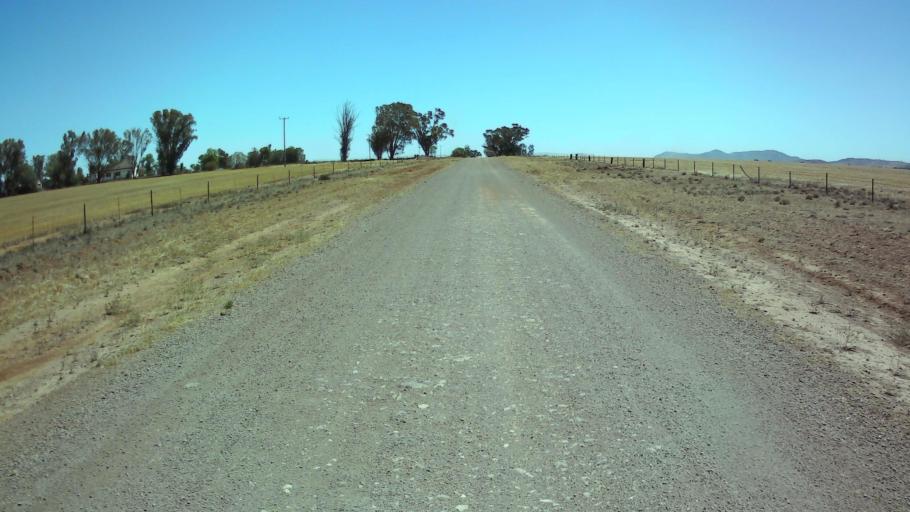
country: AU
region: New South Wales
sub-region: Forbes
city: Forbes
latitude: -33.6977
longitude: 147.7072
